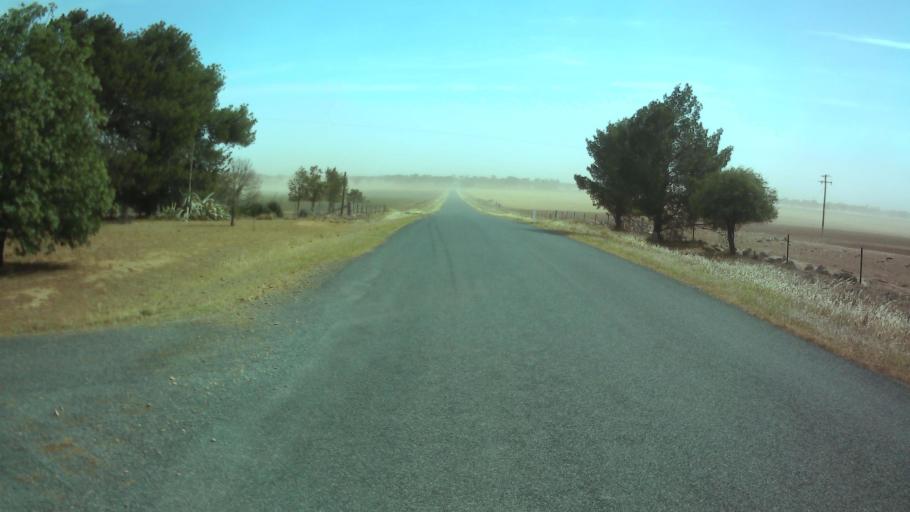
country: AU
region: New South Wales
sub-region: Weddin
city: Grenfell
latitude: -33.7301
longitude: 147.9981
